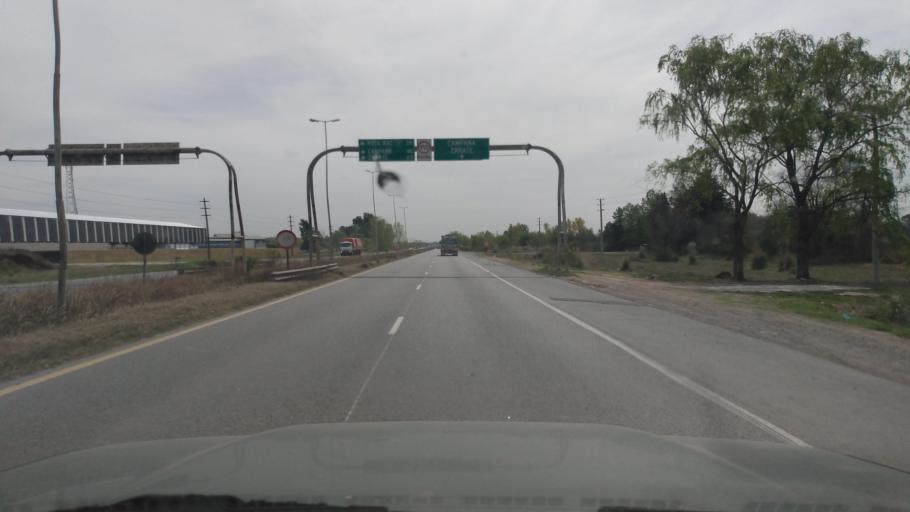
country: AR
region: Buenos Aires
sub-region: Partido de Lujan
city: Lujan
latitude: -34.5529
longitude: -59.0366
